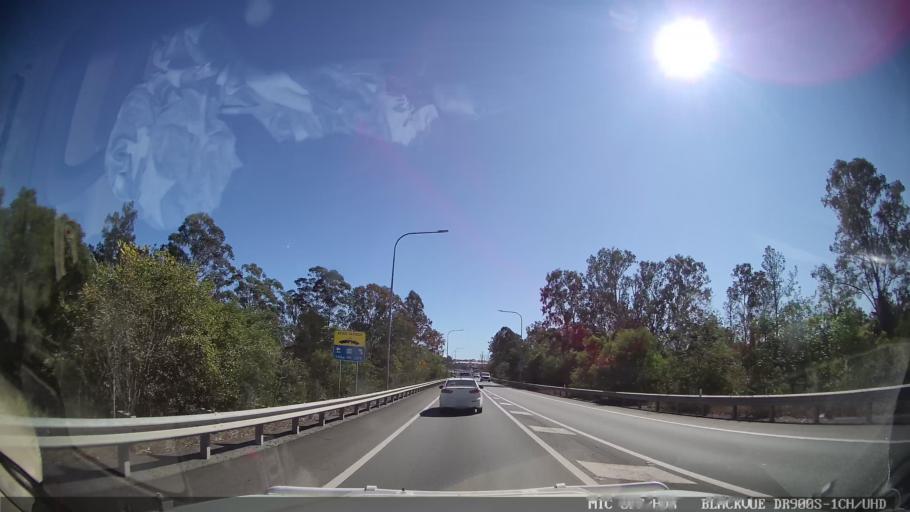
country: AU
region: Queensland
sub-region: Gympie Regional Council
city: Monkland
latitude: -26.2340
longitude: 152.6983
